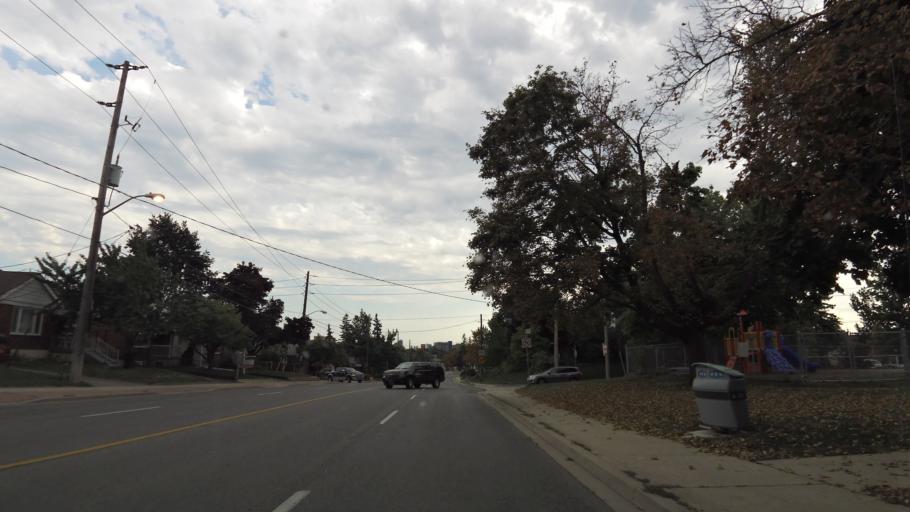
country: CA
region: Ontario
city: Toronto
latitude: 43.6933
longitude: -79.4746
